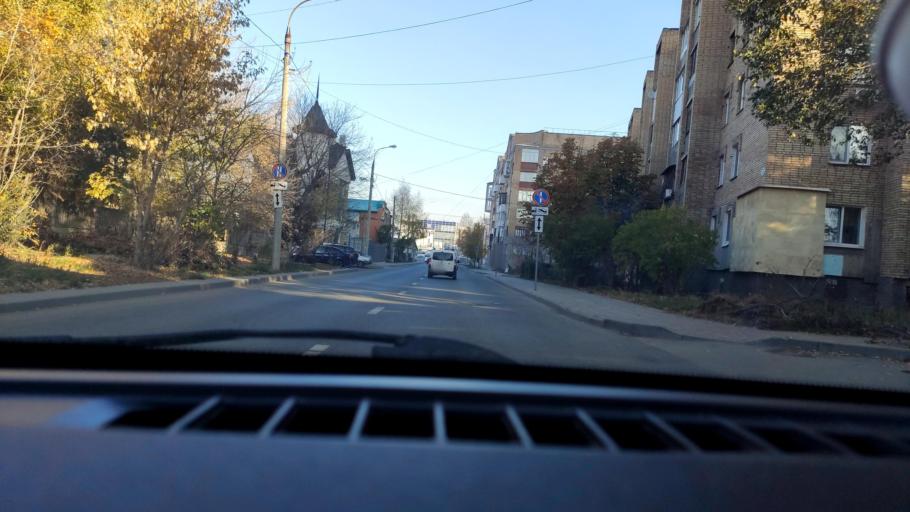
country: RU
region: Samara
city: Rozhdestveno
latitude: 53.1814
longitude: 50.0753
